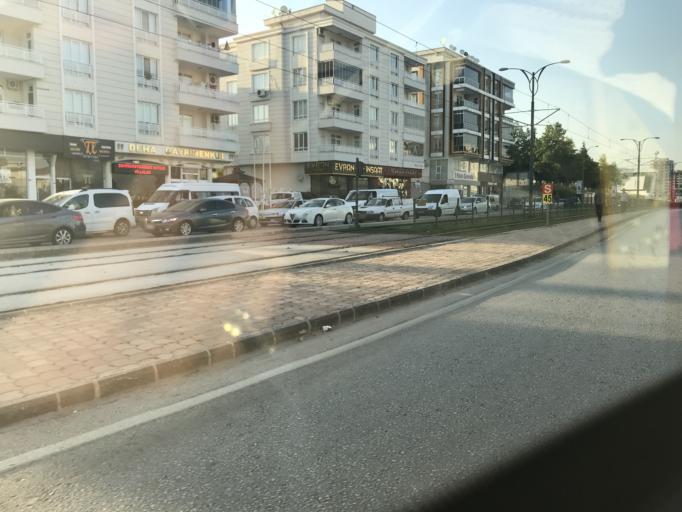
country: TR
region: Gaziantep
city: Sahinbey
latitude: 37.0569
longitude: 37.3312
